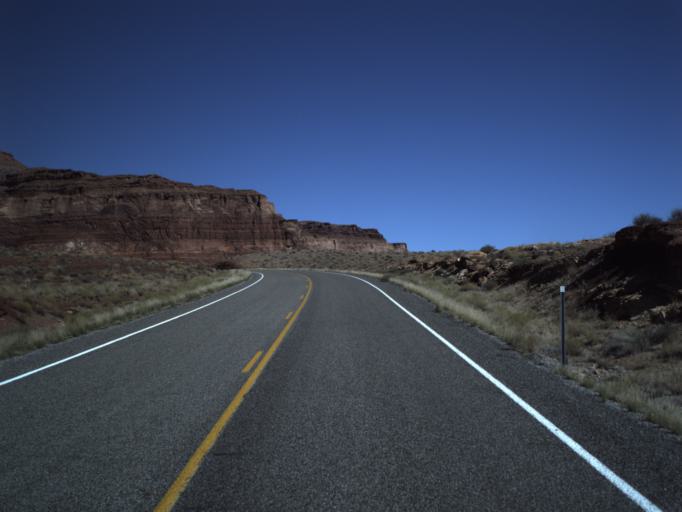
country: US
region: Utah
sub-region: San Juan County
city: Blanding
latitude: 37.9124
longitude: -110.3985
